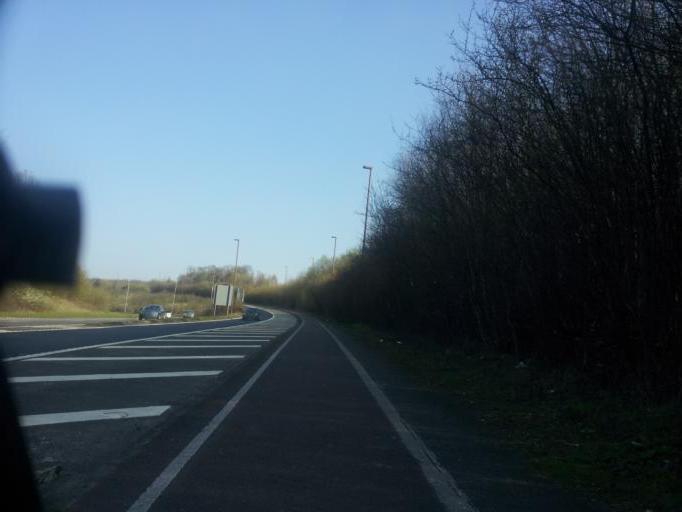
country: GB
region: England
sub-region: Medway
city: Cuxton
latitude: 51.3987
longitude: 0.4385
